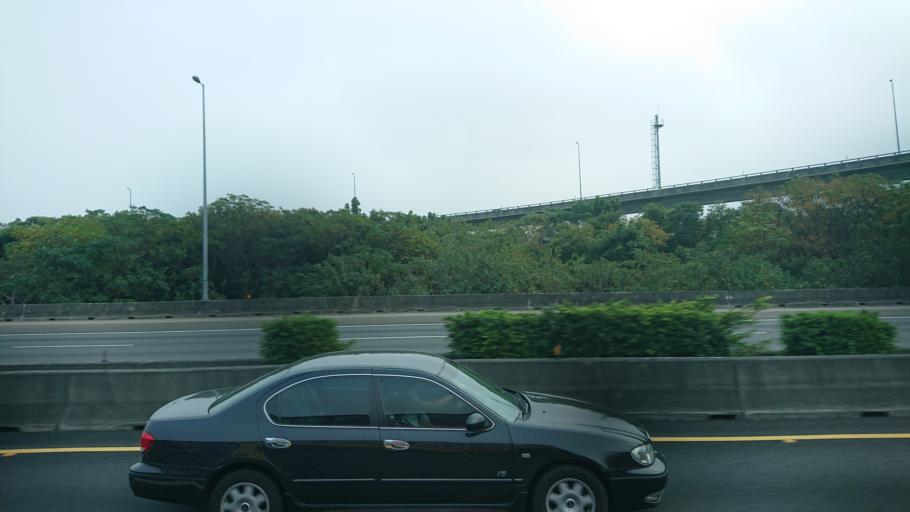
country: TW
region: Taiwan
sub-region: Changhua
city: Chang-hua
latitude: 24.1002
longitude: 120.5556
